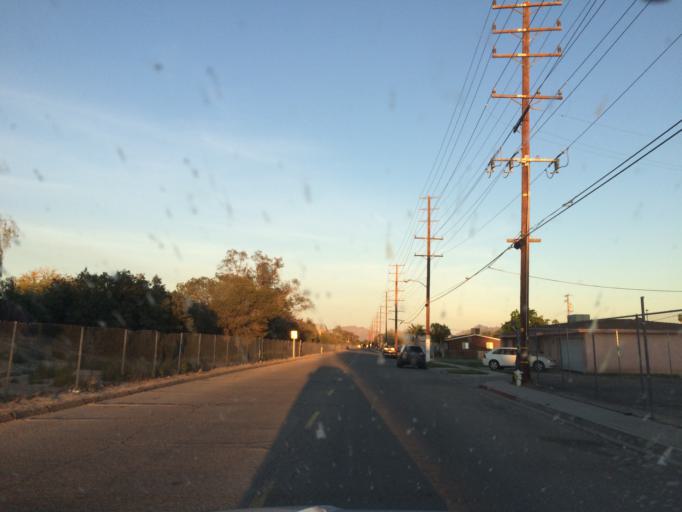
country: US
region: California
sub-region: Riverside County
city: Blythe
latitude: 33.6067
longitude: -114.5963
